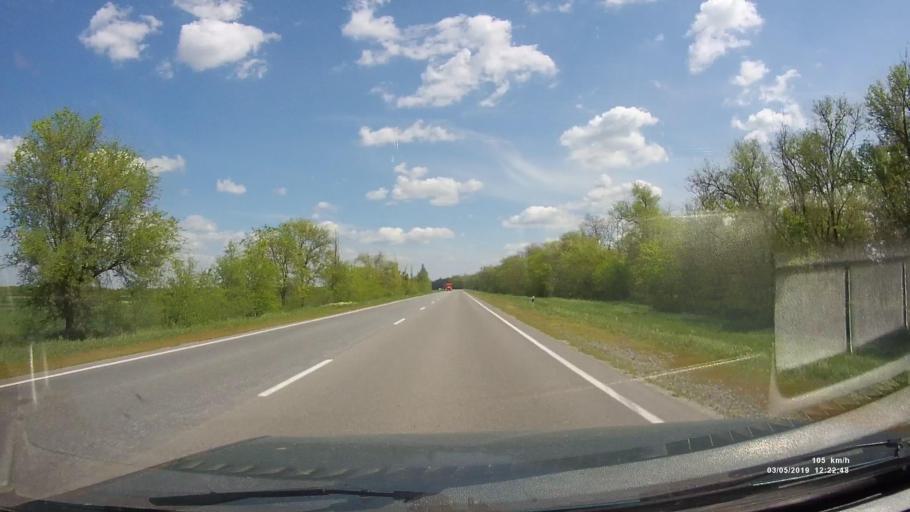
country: RU
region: Rostov
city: Semikarakorsk
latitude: 47.4066
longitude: 40.6693
